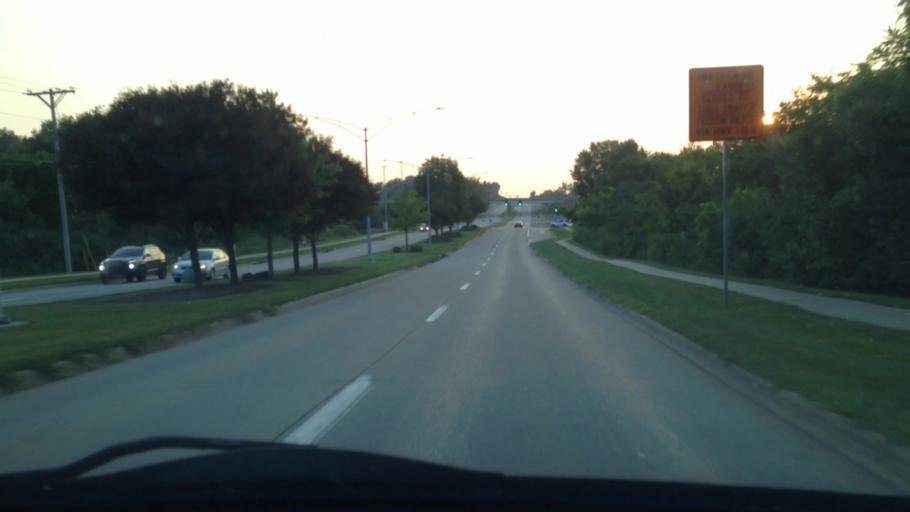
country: US
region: Iowa
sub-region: Johnson County
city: Coralville
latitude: 41.6571
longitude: -91.5916
